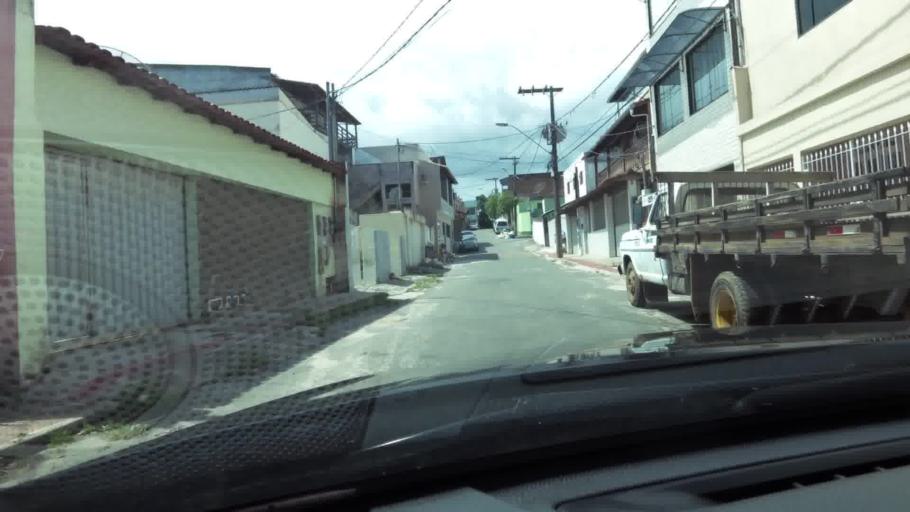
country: BR
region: Espirito Santo
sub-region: Guarapari
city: Guarapari
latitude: -20.6600
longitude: -40.5030
